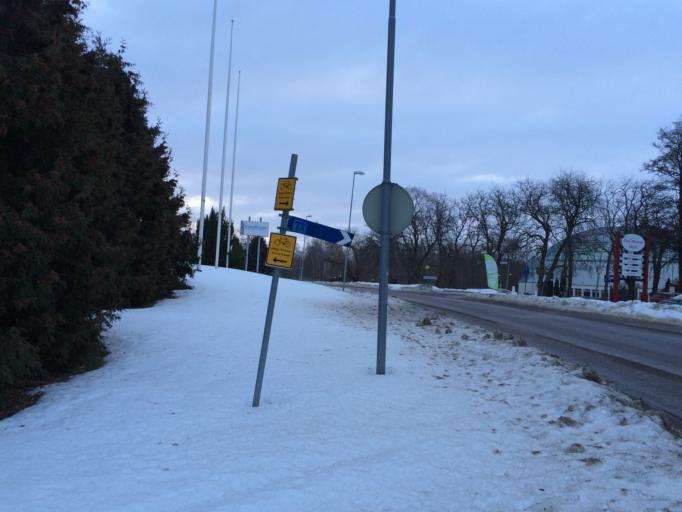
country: SE
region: Vaestmanland
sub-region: Hallstahammars Kommun
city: Hallstahammar
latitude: 59.6166
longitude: 16.2093
